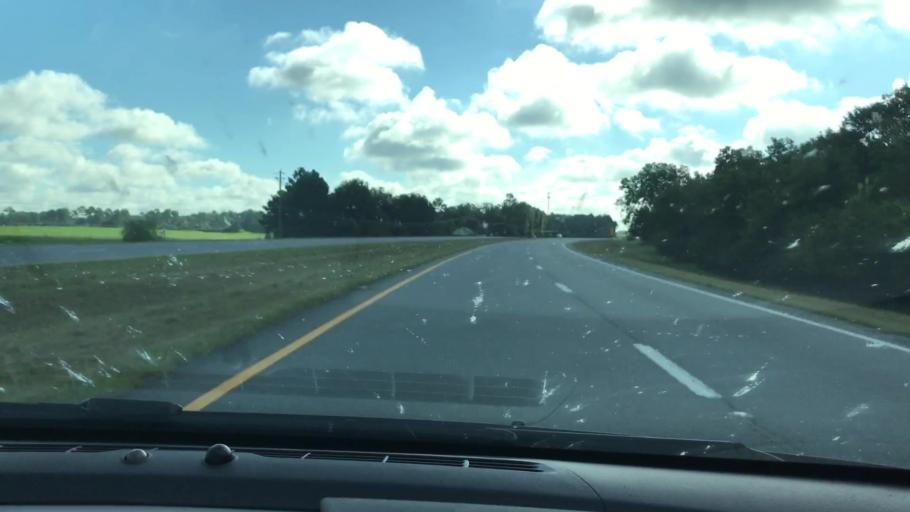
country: US
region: Georgia
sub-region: Worth County
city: Sylvester
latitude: 31.5530
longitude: -83.9520
